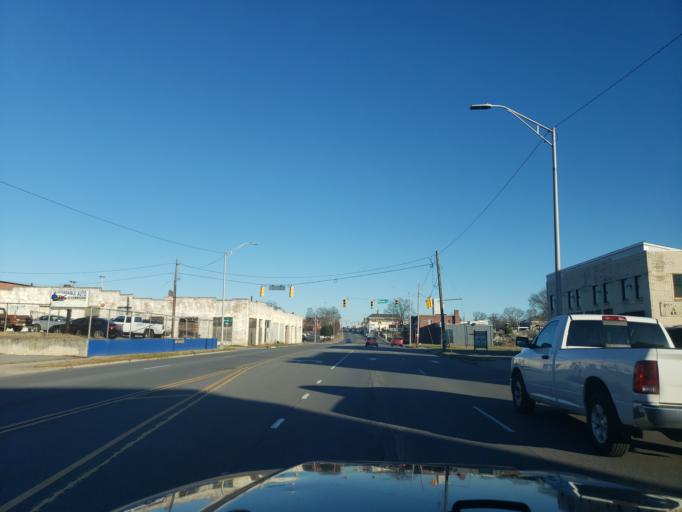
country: US
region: North Carolina
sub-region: Gaston County
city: Gastonia
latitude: 35.2622
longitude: -81.1910
